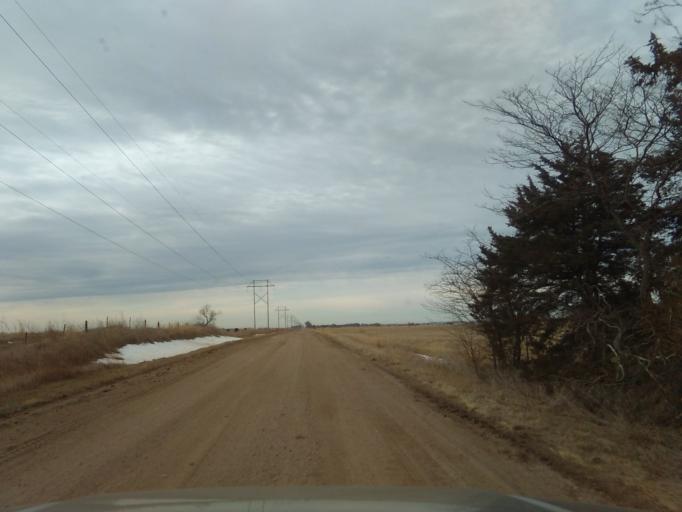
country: US
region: Nebraska
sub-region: Buffalo County
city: Shelton
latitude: 40.6548
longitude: -98.7302
